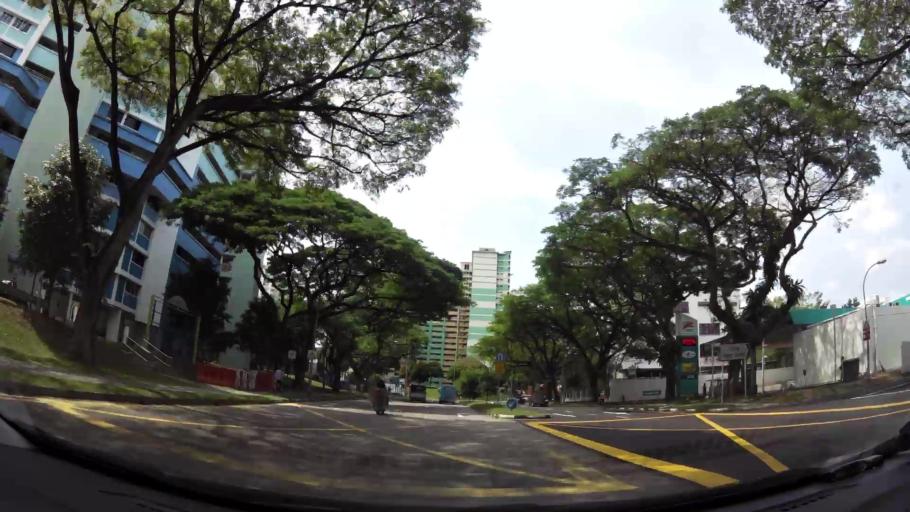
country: MY
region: Johor
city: Johor Bahru
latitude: 1.3495
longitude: 103.7152
